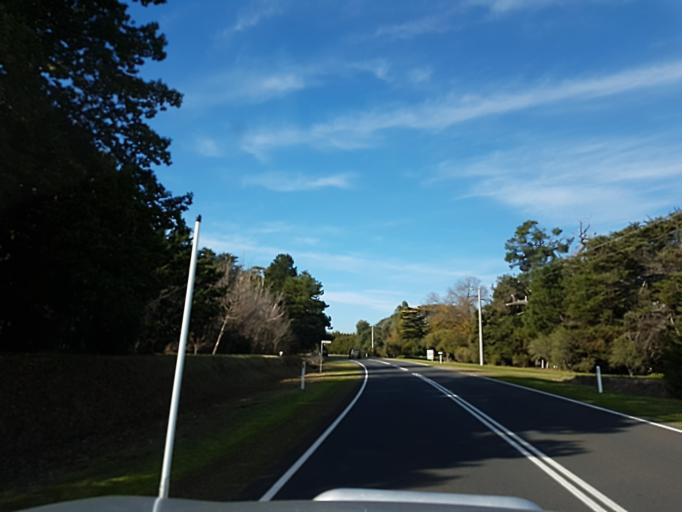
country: AU
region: Victoria
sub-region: Murrindindi
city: Alexandra
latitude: -37.1505
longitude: 145.5993
